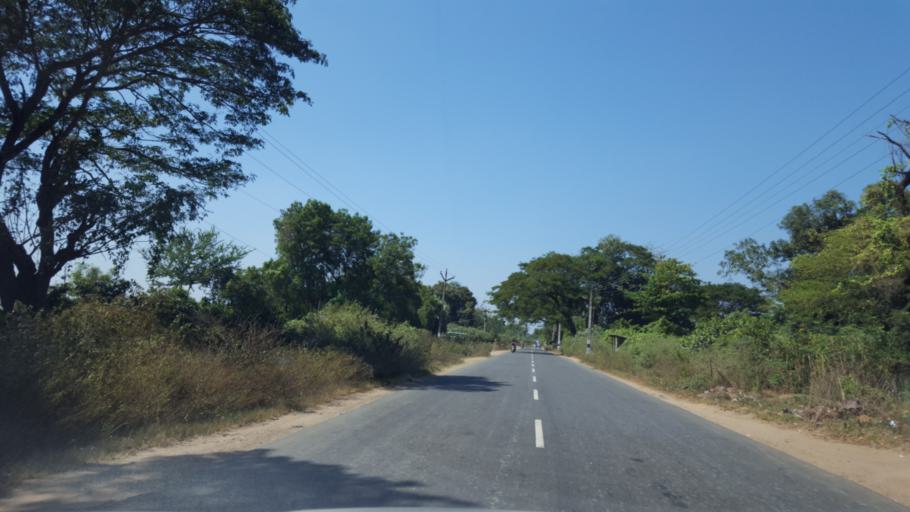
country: IN
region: Tamil Nadu
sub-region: Kancheepuram
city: Chengalpattu
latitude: 12.7227
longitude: 79.9529
